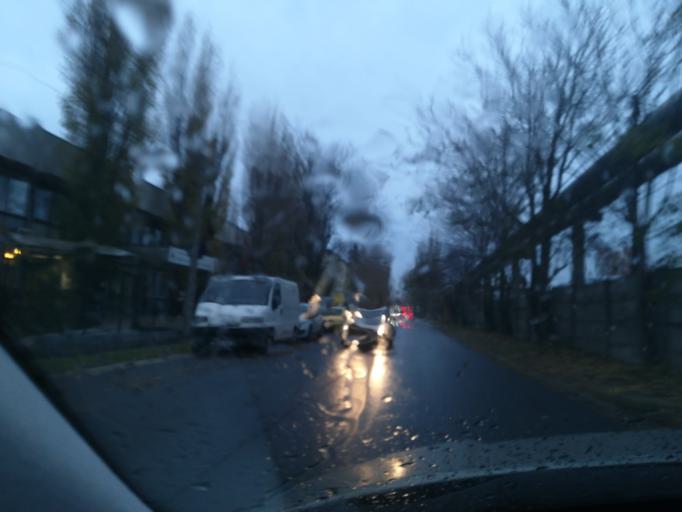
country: HU
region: Budapest
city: Budapest III. keruelet
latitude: 47.5532
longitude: 19.0337
